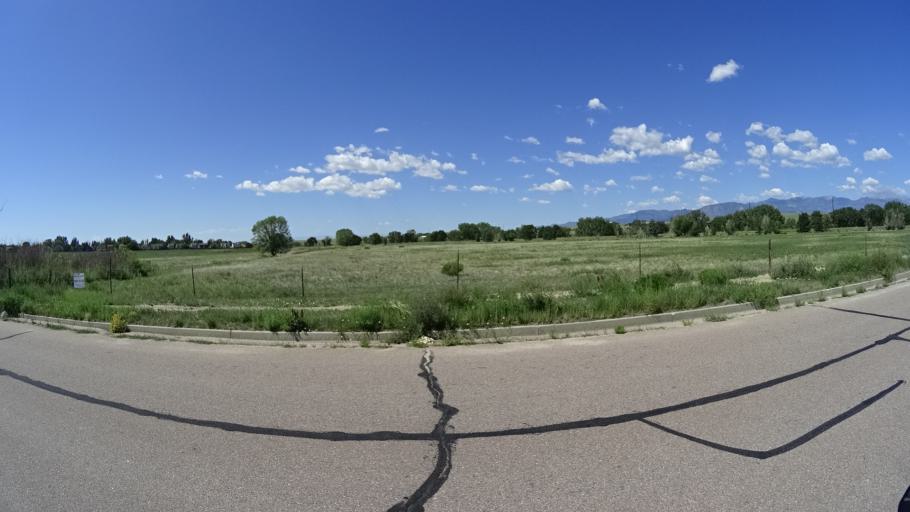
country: US
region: Colorado
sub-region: El Paso County
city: Security-Widefield
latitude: 38.7737
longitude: -104.6570
